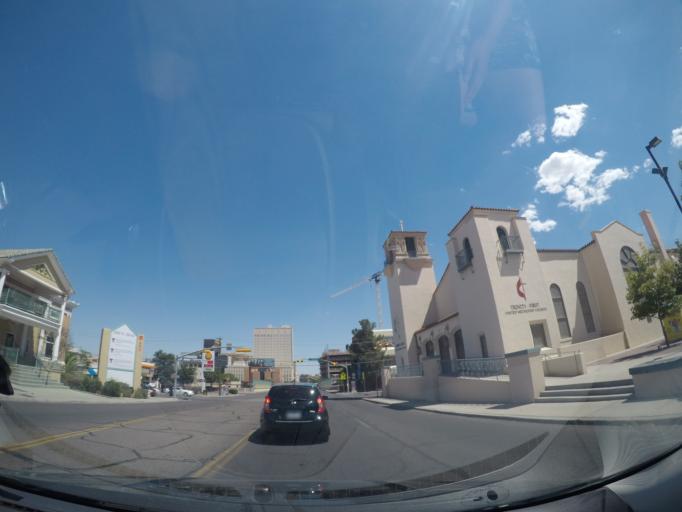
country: US
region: Texas
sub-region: El Paso County
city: El Paso
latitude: 31.7635
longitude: -106.4913
